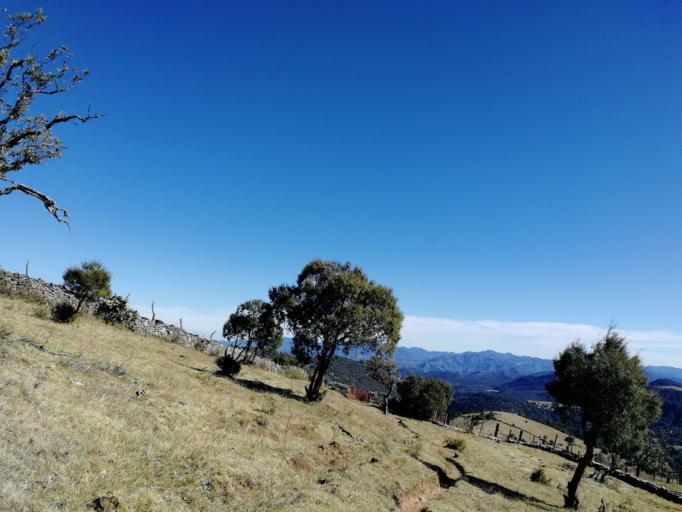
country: MX
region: San Luis Potosi
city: Zaragoza
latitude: 22.0047
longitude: -100.6120
